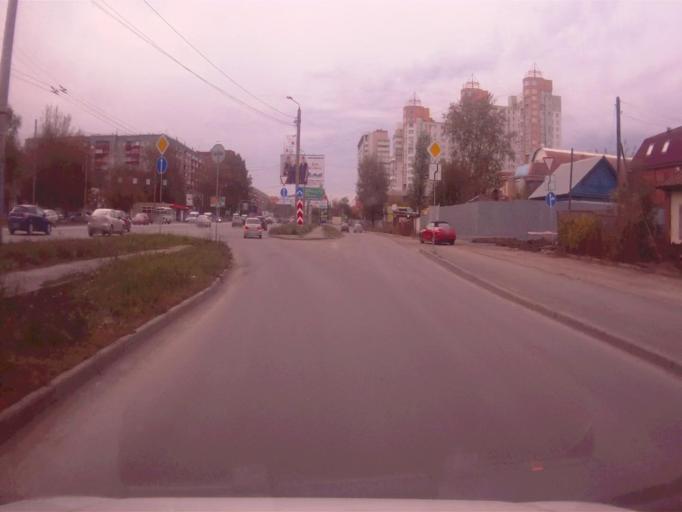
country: RU
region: Chelyabinsk
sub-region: Gorod Chelyabinsk
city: Chelyabinsk
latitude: 55.1788
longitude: 61.3563
